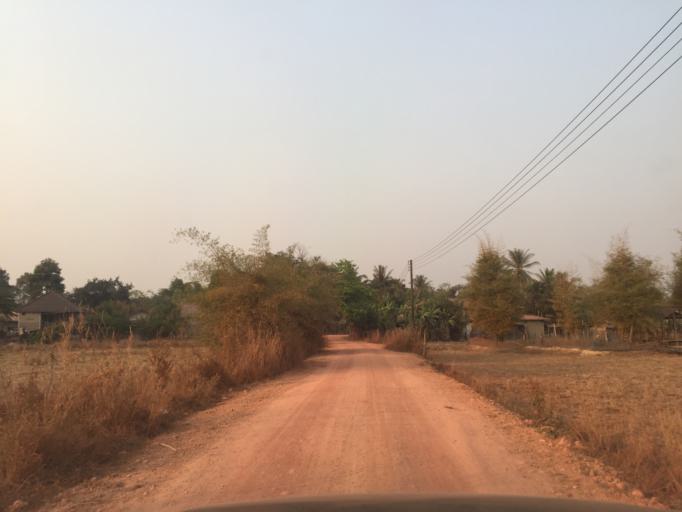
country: LA
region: Vientiane
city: Vientiane
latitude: 18.0611
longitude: 102.5210
